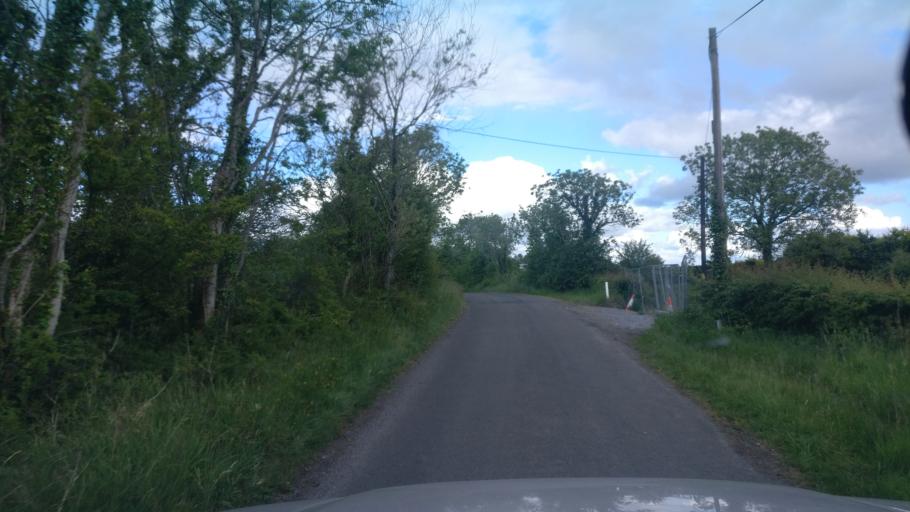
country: IE
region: Connaught
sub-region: County Galway
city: Portumna
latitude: 53.1991
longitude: -8.3293
